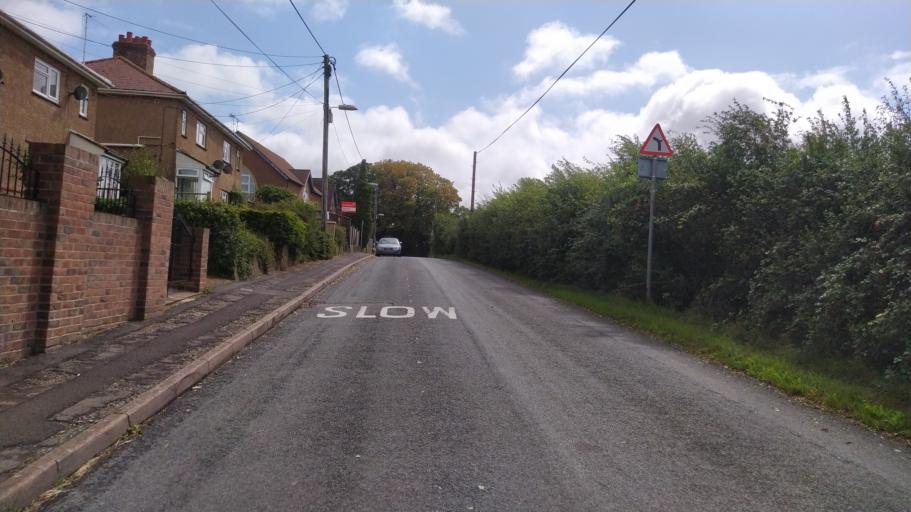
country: GB
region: England
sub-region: Wiltshire
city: Bower Chalke
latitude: 50.9547
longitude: -2.0106
